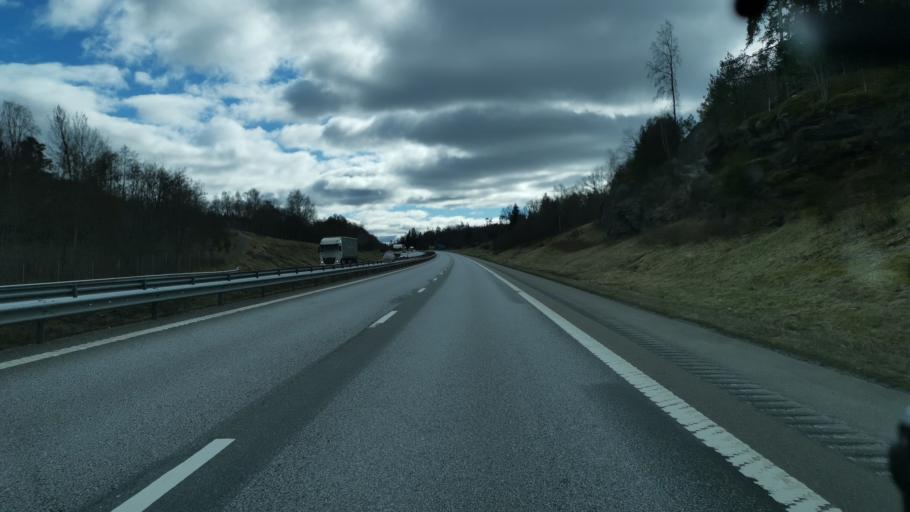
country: SE
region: Vaestra Goetaland
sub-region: Uddevalla Kommun
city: Uddevalla
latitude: 58.3038
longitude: 11.8594
